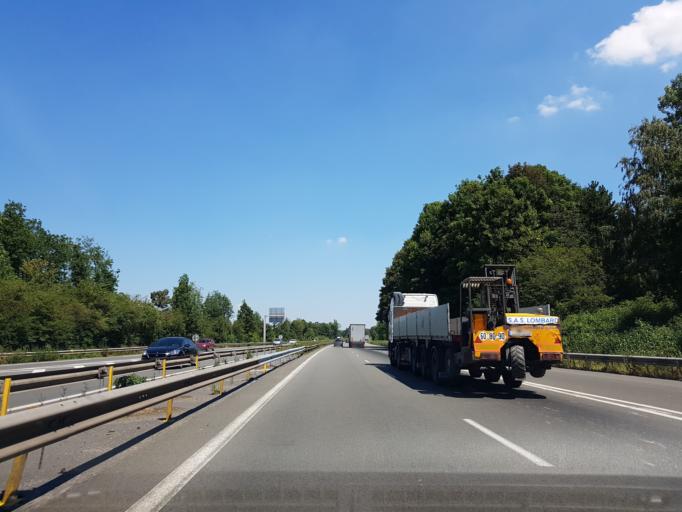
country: FR
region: Nord-Pas-de-Calais
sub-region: Departement du Nord
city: Lieu-Saint-Amand
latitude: 50.2699
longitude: 3.3341
